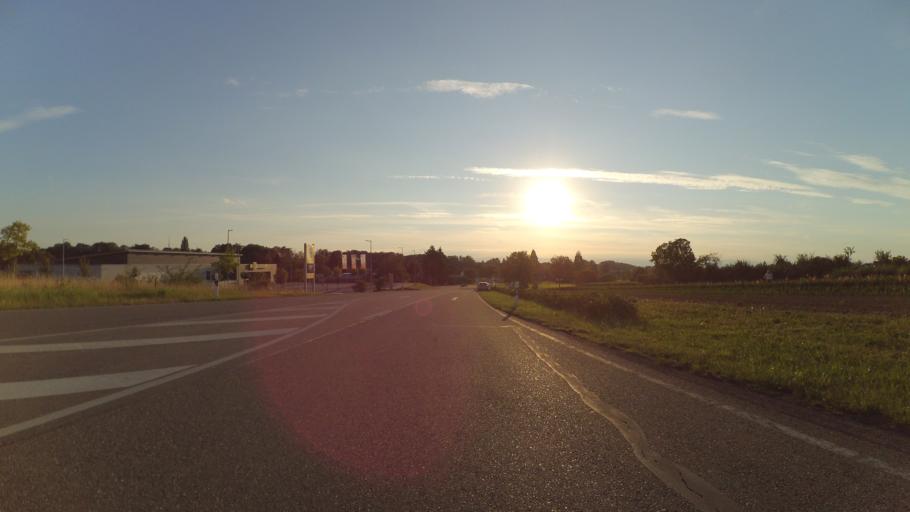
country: DE
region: Baden-Wuerttemberg
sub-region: Freiburg Region
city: Sulzburg
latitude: 47.8540
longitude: 7.6978
